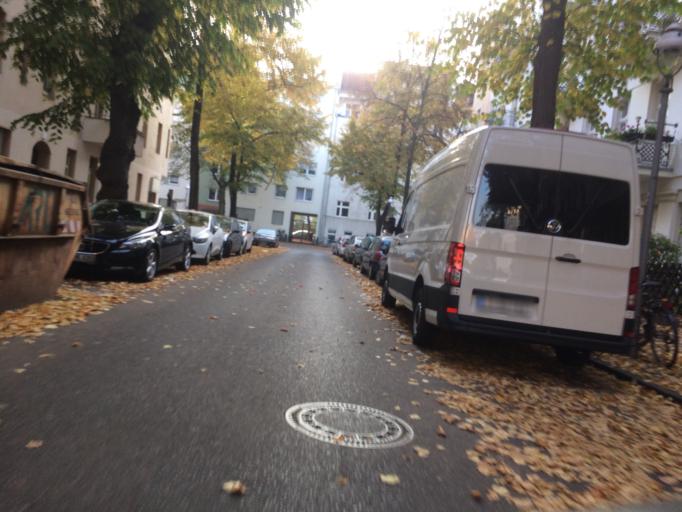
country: DE
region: Berlin
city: Pankow
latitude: 52.5647
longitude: 13.3895
